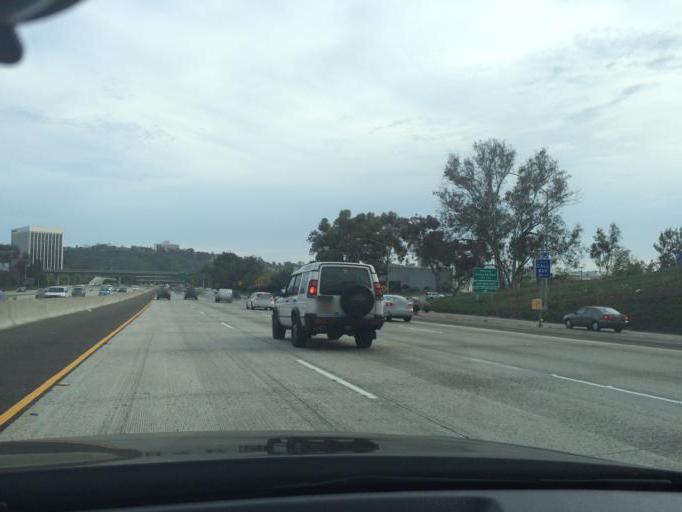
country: US
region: California
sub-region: San Diego County
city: San Diego
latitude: 32.7714
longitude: -117.1614
